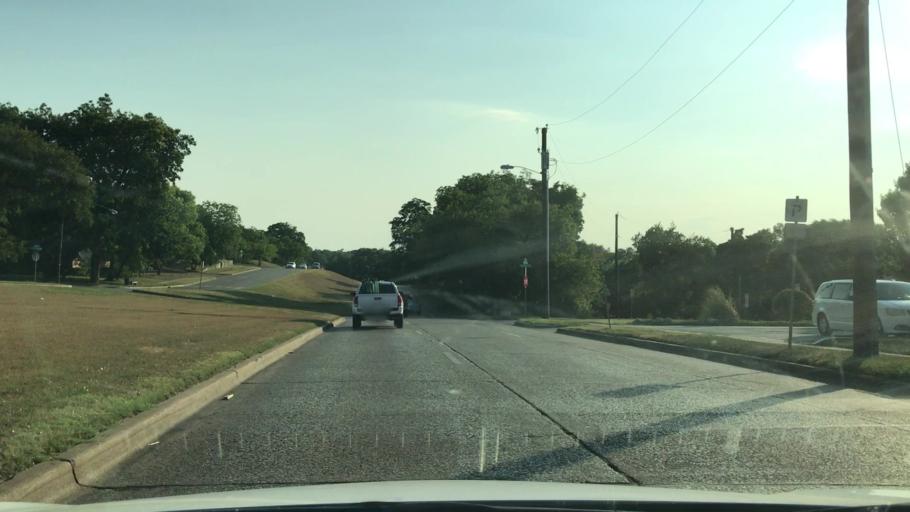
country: US
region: Texas
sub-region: Dallas County
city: Cockrell Hill
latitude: 32.7473
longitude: -96.8638
